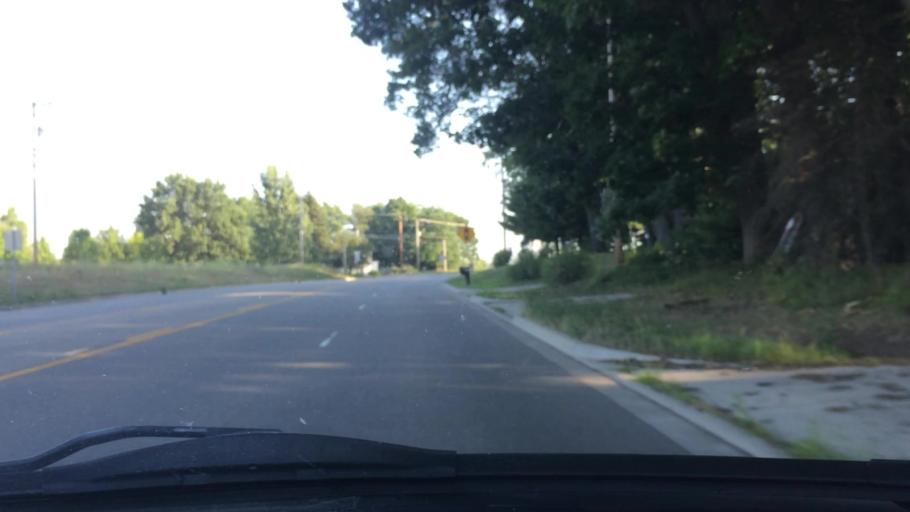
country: US
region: Indiana
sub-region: Saint Joseph County
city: Granger
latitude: 41.7261
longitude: -86.1587
